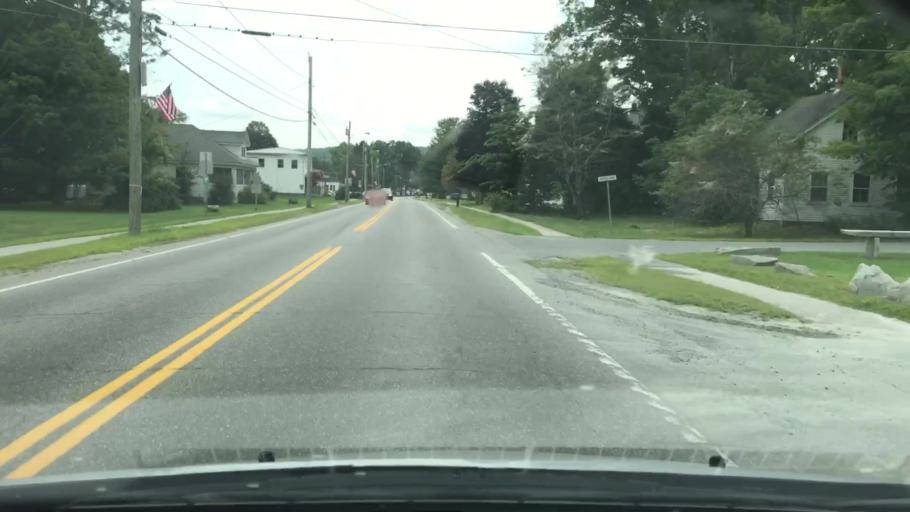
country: US
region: New Hampshire
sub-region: Grafton County
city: North Haverhill
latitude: 44.0881
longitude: -72.0260
